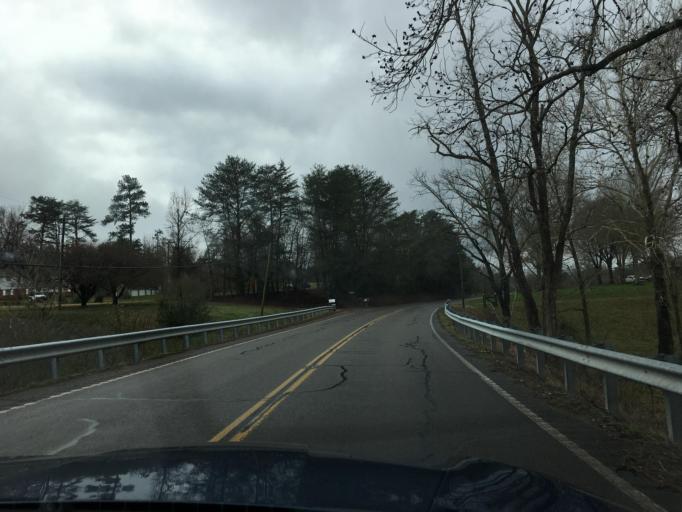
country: US
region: Tennessee
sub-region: Polk County
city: Benton
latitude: 35.1338
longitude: -84.6433
